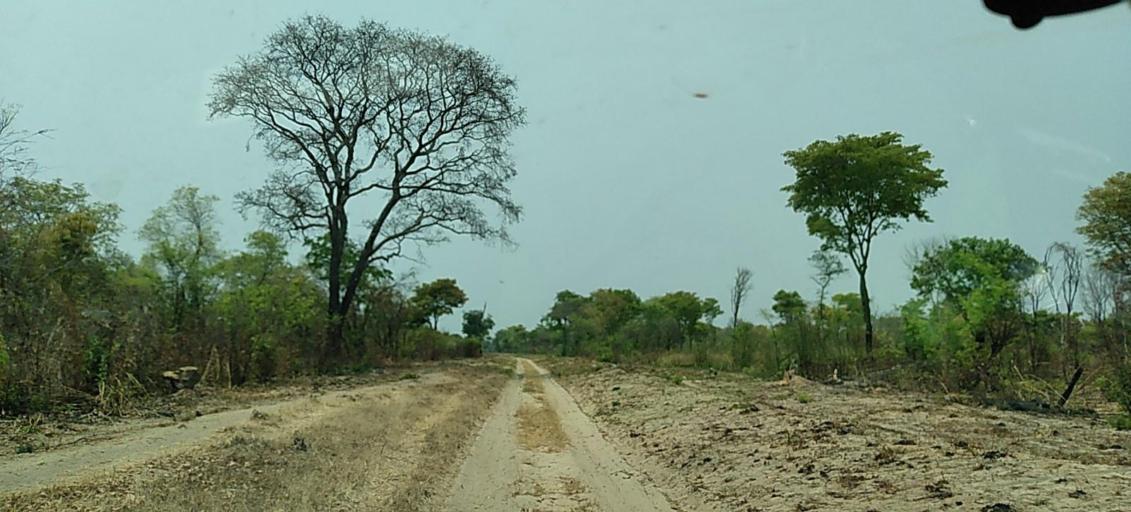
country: ZM
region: Western
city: Lukulu
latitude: -14.1462
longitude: 23.2893
